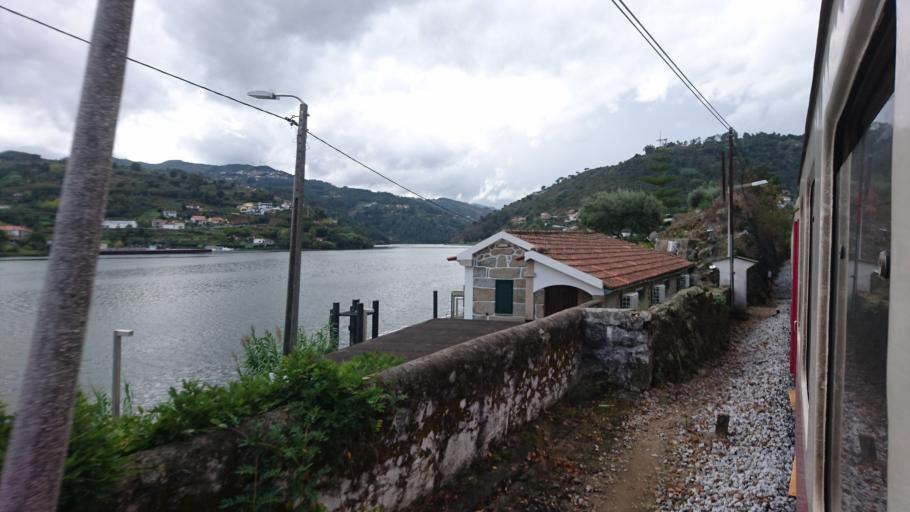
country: PT
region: Viseu
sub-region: Resende
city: Resende
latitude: 41.1063
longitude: -8.0091
